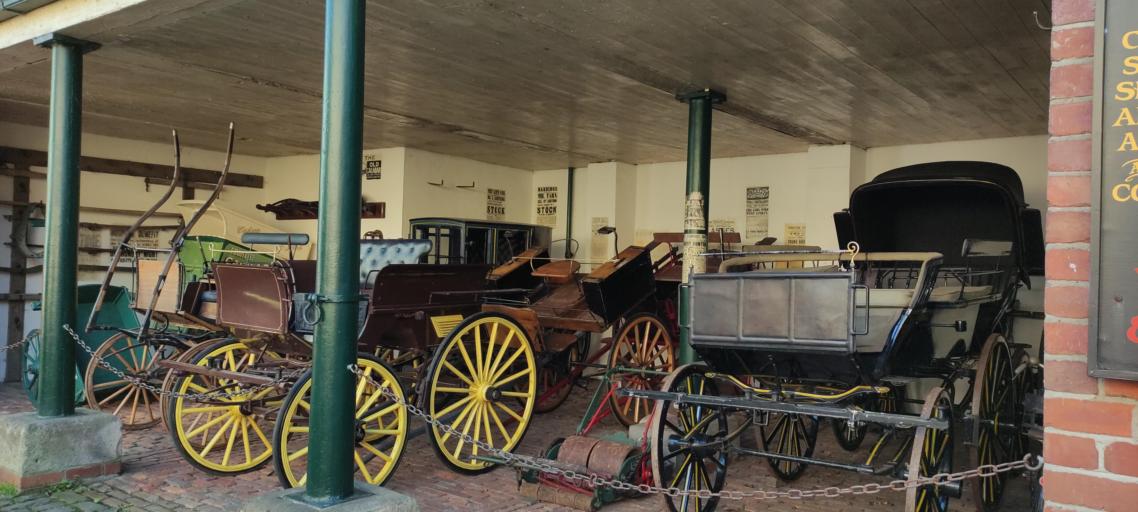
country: GB
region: England
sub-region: County Durham
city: Stanley
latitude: 54.8895
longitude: -1.6611
